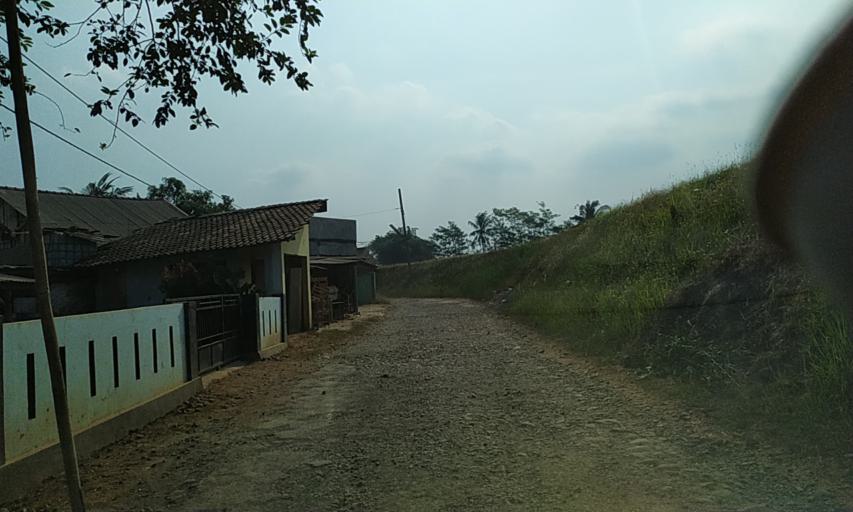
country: ID
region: Central Java
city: Bojongsari
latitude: -7.3189
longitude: 108.7654
